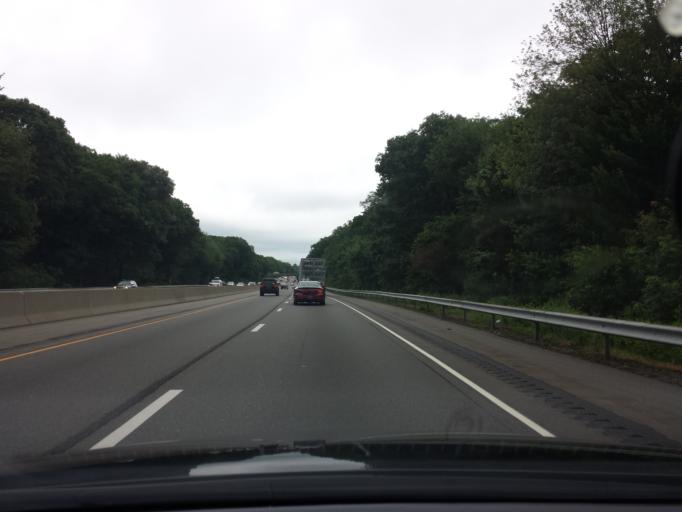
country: US
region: Connecticut
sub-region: Middlesex County
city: Clinton
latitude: 41.2881
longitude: -72.5553
